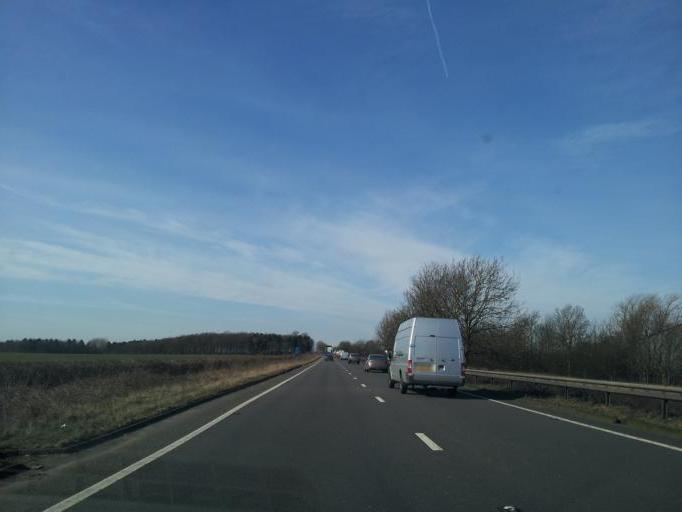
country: GB
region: England
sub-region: District of Rutland
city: Clipsham
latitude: 52.7027
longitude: -0.5815
